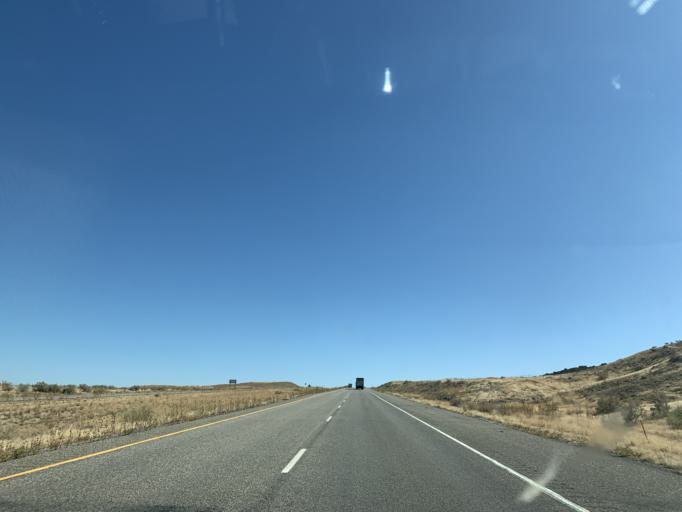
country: US
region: Colorado
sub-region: Mesa County
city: Loma
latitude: 39.2204
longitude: -108.8843
